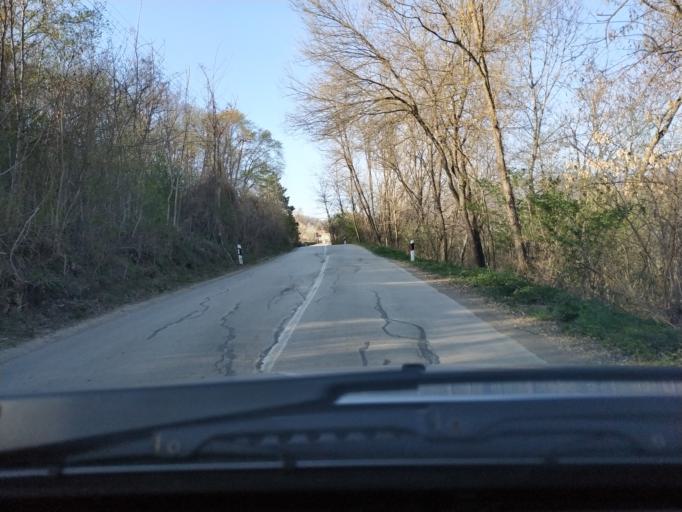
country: RS
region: Central Serbia
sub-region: Nisavski Okrug
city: Aleksinac
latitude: 43.5176
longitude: 21.7995
